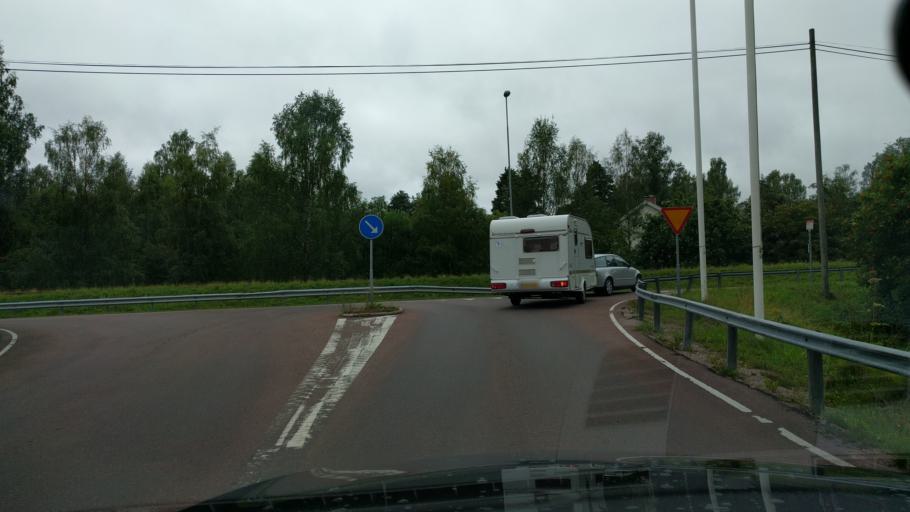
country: SE
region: Dalarna
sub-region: Mora Kommun
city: Mora
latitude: 61.0073
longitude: 14.5180
